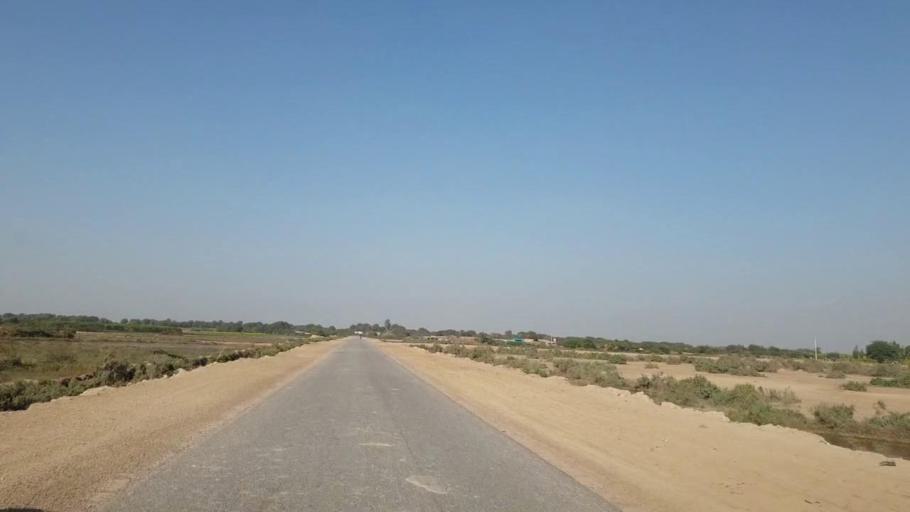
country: PK
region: Sindh
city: Digri
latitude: 25.1170
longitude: 69.1081
